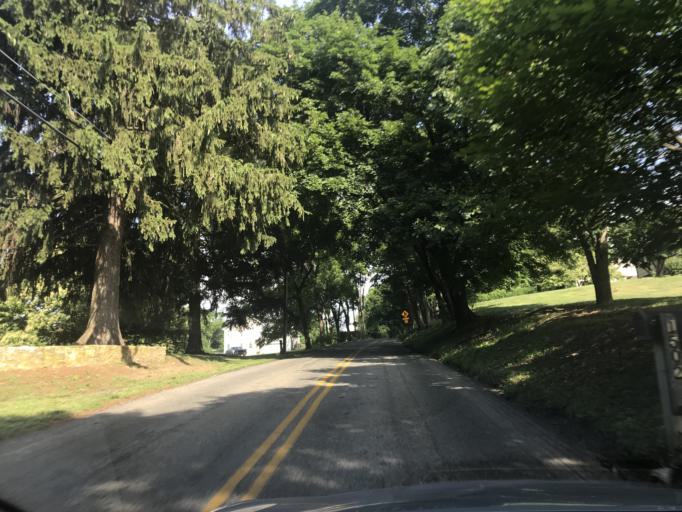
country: US
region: Maryland
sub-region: Harford County
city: Bel Air North
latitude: 39.5567
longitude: -76.4118
